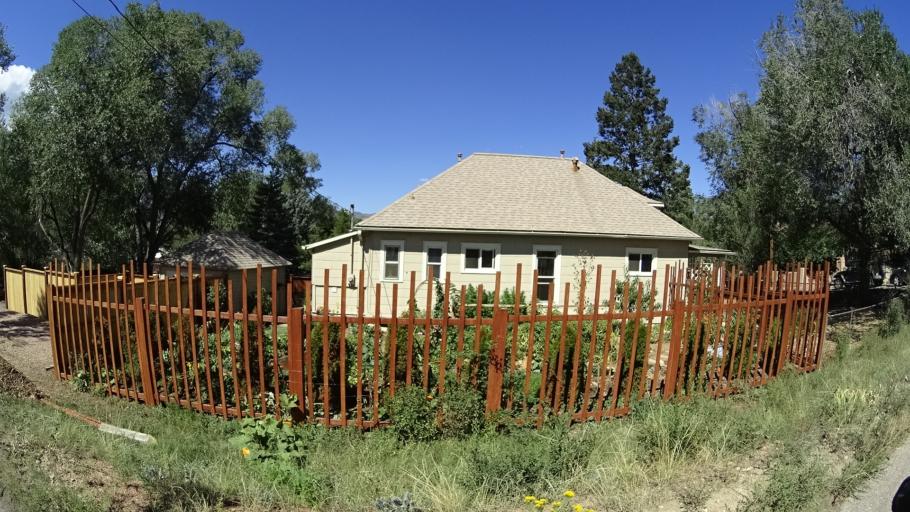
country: US
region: Colorado
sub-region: El Paso County
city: Colorado Springs
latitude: 38.8518
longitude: -104.8533
